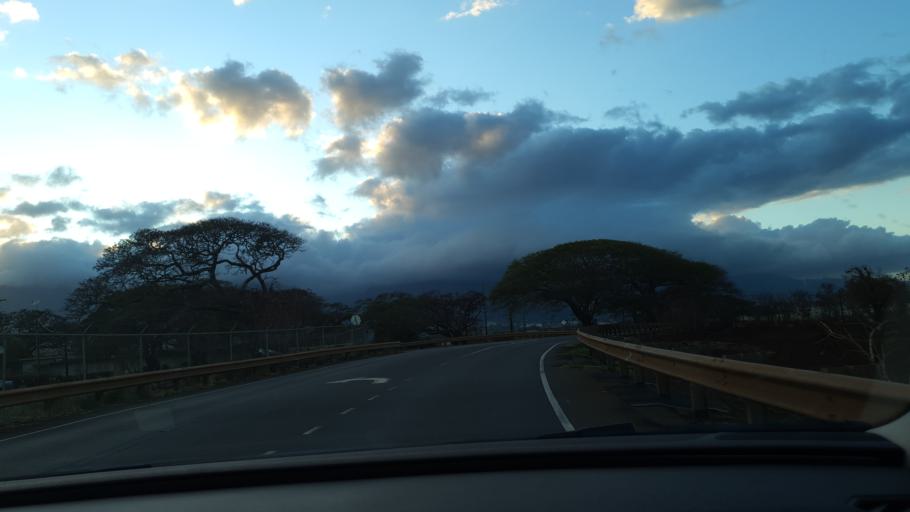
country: US
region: Hawaii
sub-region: Maui County
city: Kahului
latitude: 20.8692
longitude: -156.4517
